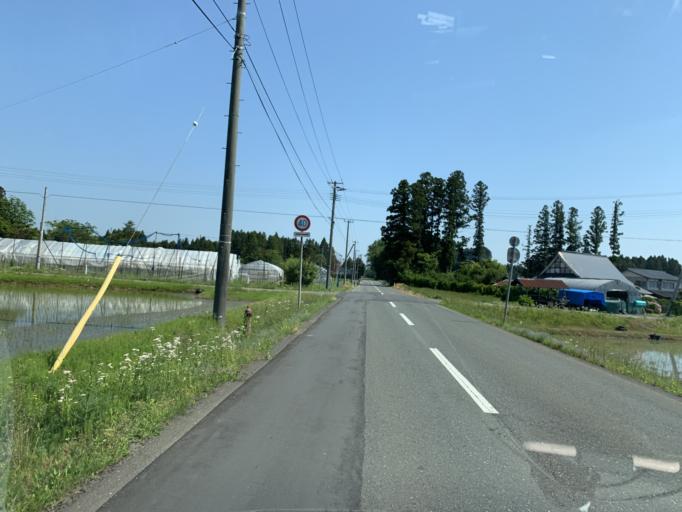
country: JP
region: Iwate
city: Mizusawa
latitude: 39.0842
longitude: 141.0674
